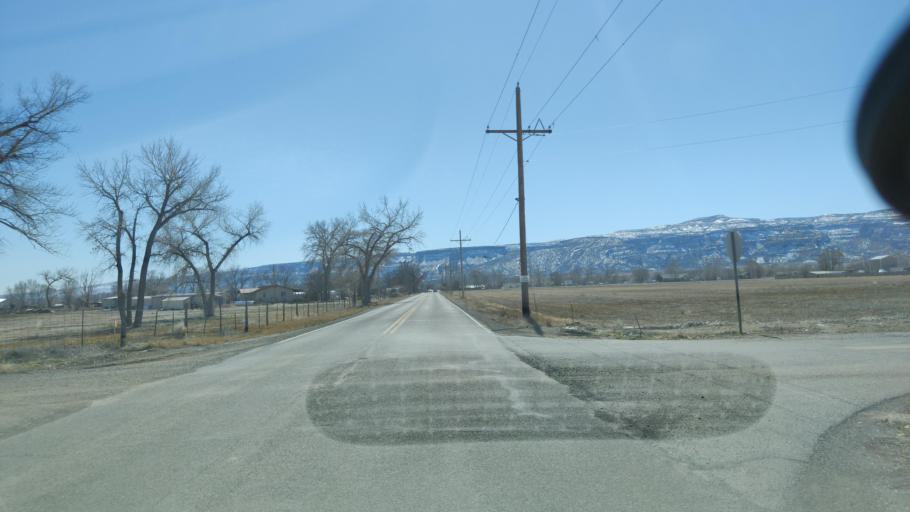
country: US
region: Colorado
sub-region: Mesa County
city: Fruita
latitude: 39.1536
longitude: -108.7011
